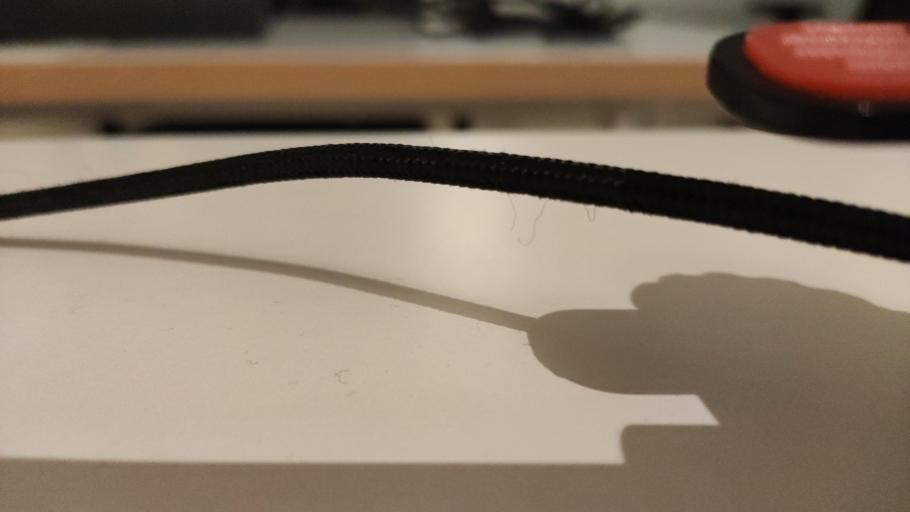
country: RU
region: Moskovskaya
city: Likino-Dulevo
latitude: 55.6969
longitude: 38.9541
